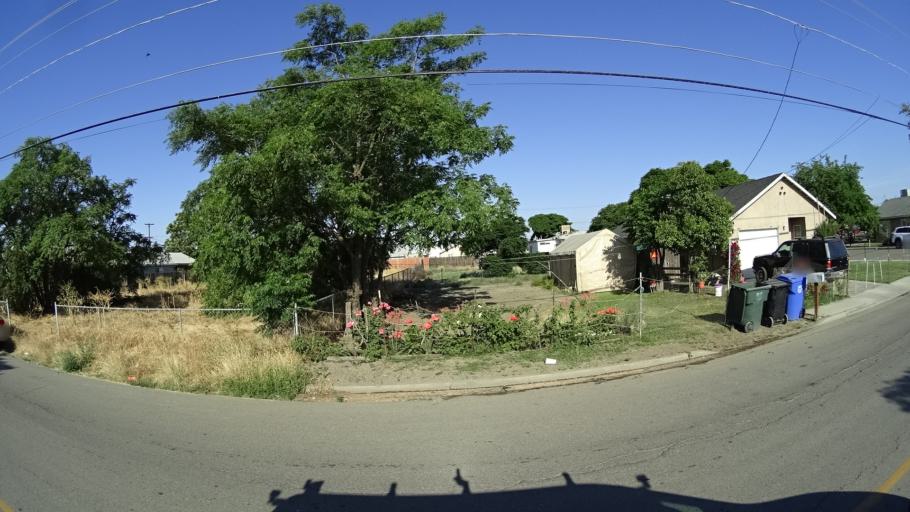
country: US
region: California
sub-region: Kings County
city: Corcoran
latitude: 36.1034
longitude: -119.5543
